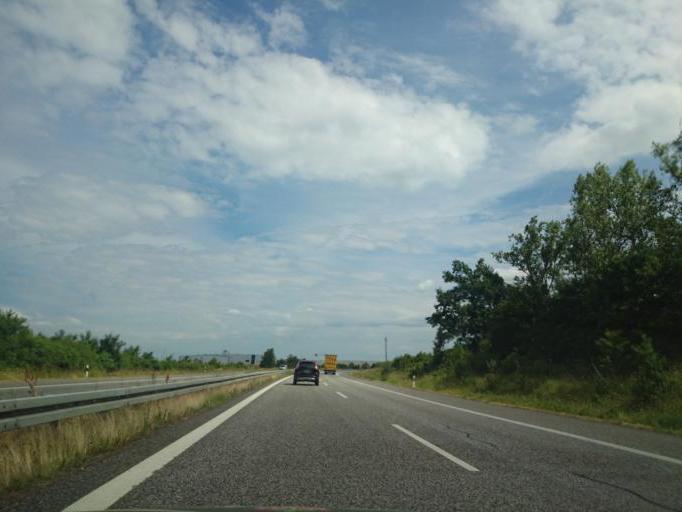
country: DE
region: Brandenburg
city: Grossbeeren
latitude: 52.3669
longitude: 13.2968
